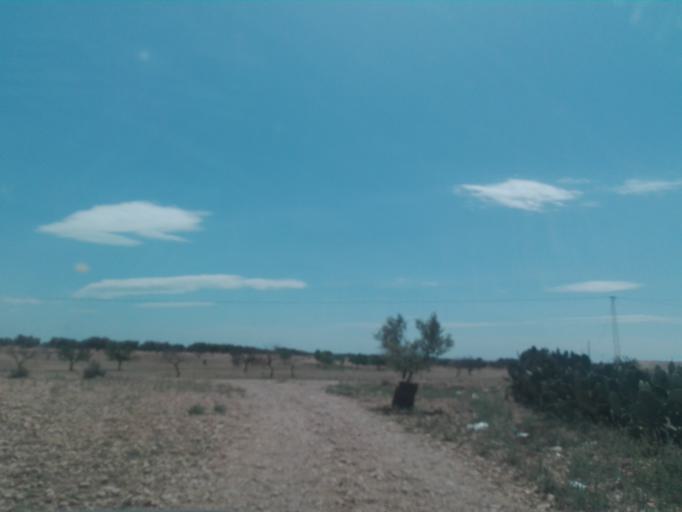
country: TN
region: Safaqis
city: Sfax
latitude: 34.6543
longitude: 10.5937
